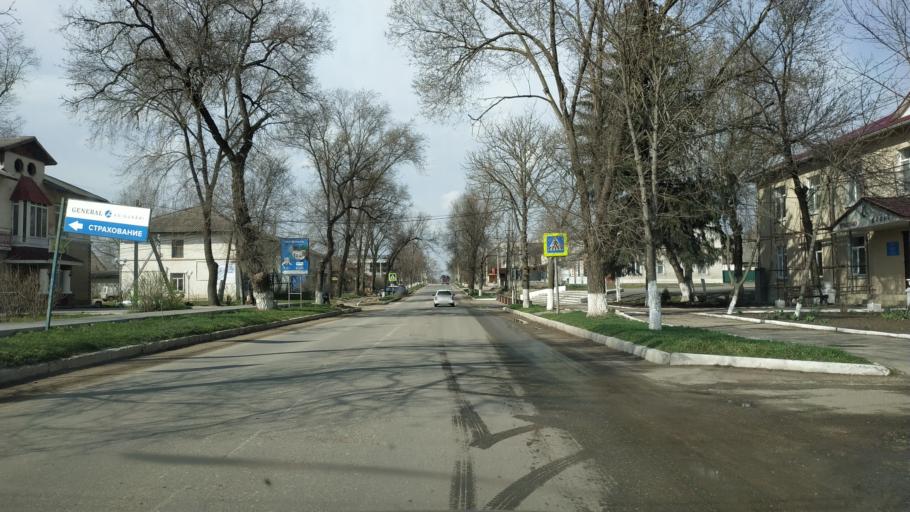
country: MD
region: Gagauzia
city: Vulcanesti
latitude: 45.6851
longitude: 28.4053
